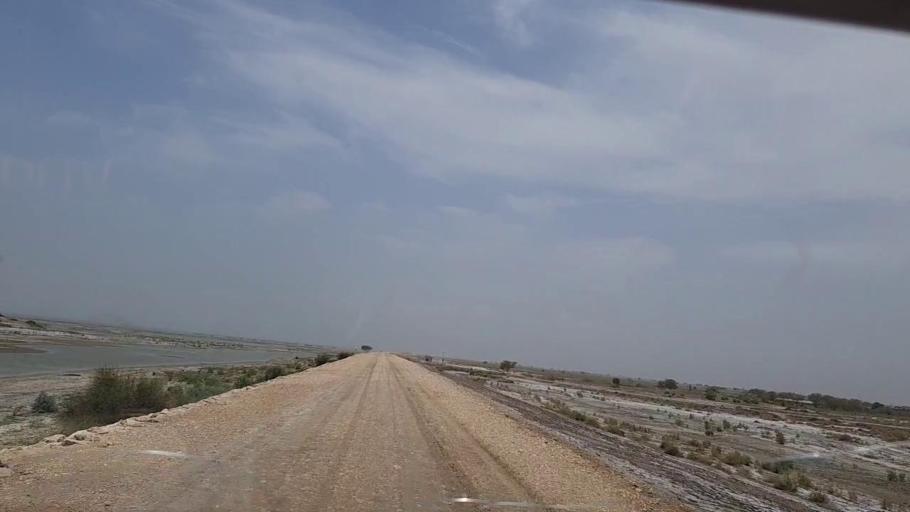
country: PK
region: Sindh
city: Sehwan
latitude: 26.4155
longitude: 67.7588
